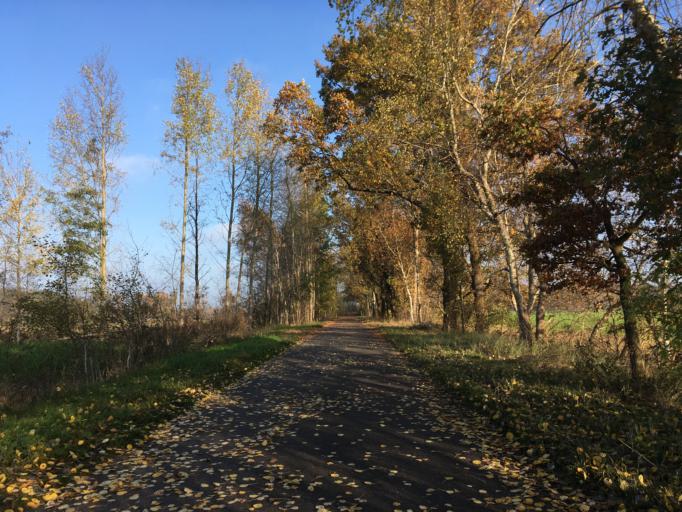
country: DE
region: Brandenburg
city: Schlepzig
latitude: 52.0406
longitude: 13.9041
